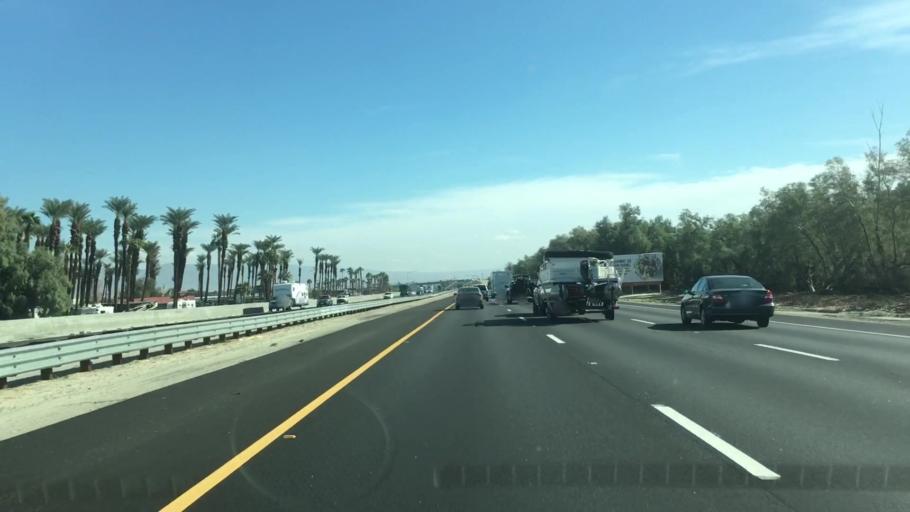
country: US
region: California
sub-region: Riverside County
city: Bermuda Dunes
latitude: 33.7635
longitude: -116.3136
